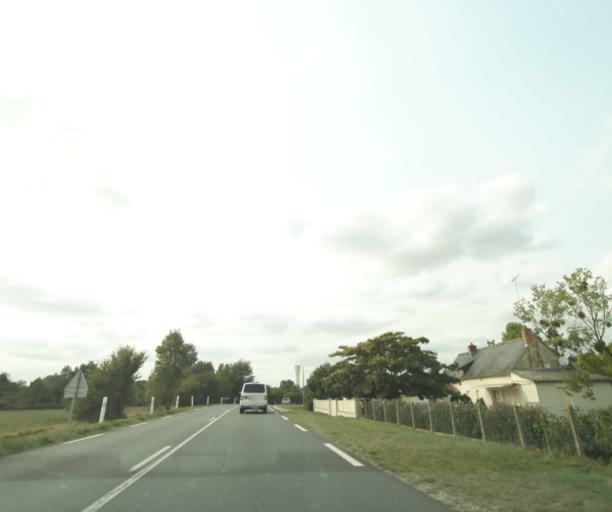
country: FR
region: Centre
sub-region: Departement de l'Indre
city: Chatillon-sur-Indre
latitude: 46.9750
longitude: 1.1837
